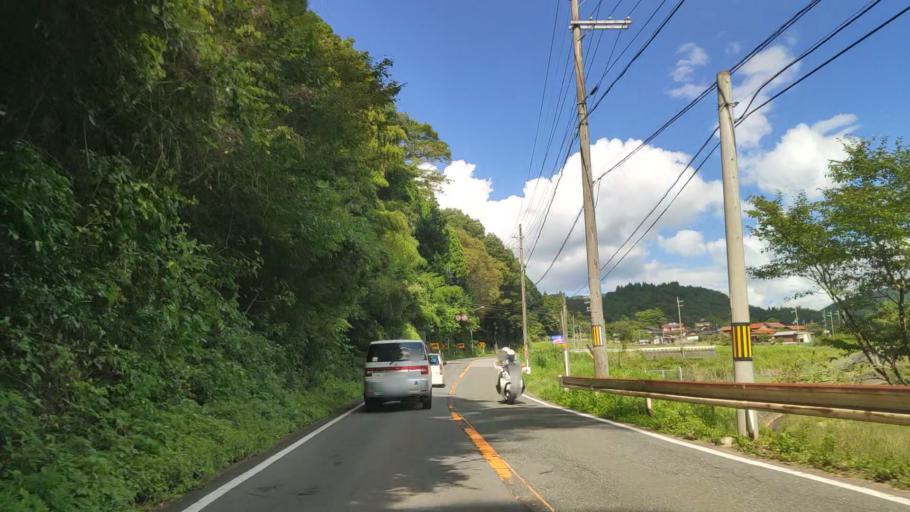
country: JP
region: Hyogo
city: Toyooka
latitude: 35.4945
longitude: 134.9595
